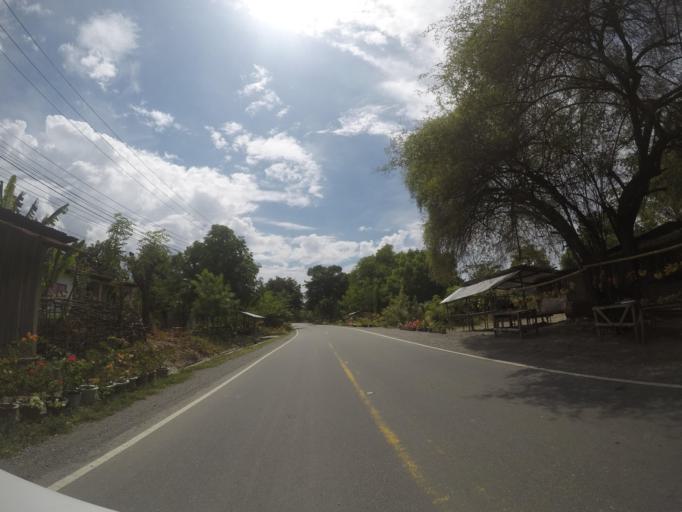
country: TL
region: Liquica
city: Liquica
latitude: -8.5813
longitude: 125.3582
